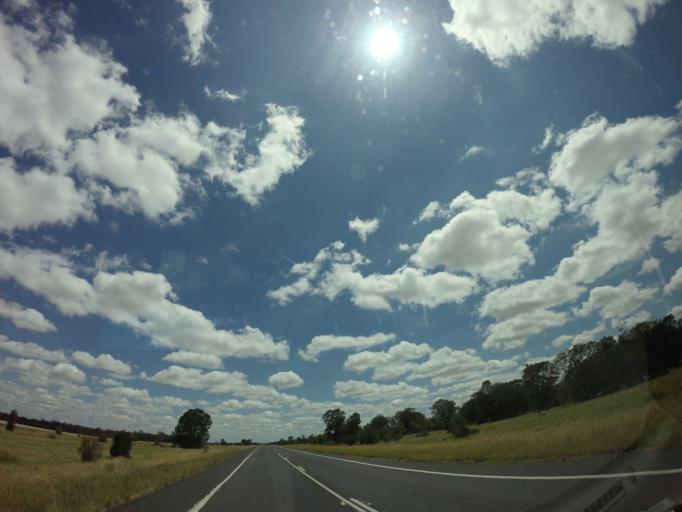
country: AU
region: New South Wales
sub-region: Moree Plains
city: Moree
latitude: -29.1469
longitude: 150.0193
